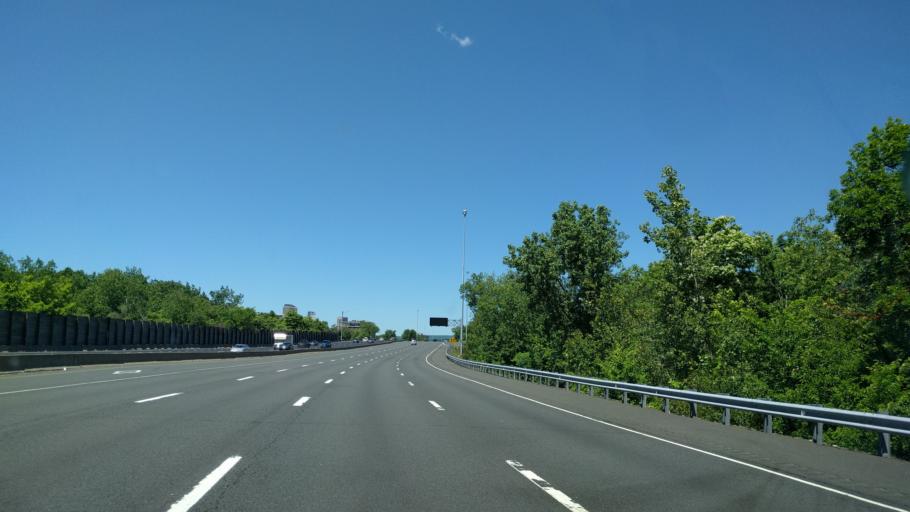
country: US
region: Connecticut
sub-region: Hartford County
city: East Hartford
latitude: 41.7636
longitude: -72.6415
